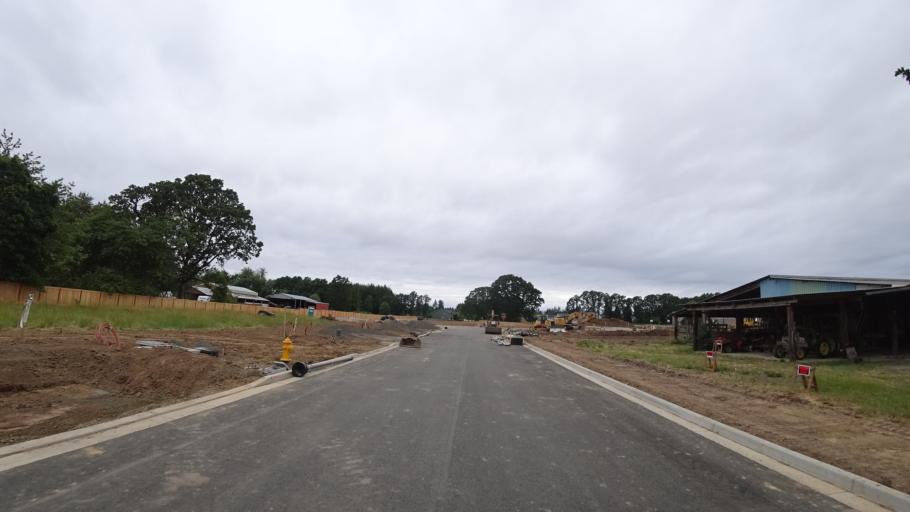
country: US
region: Oregon
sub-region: Washington County
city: Aloha
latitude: 45.4914
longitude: -122.9314
